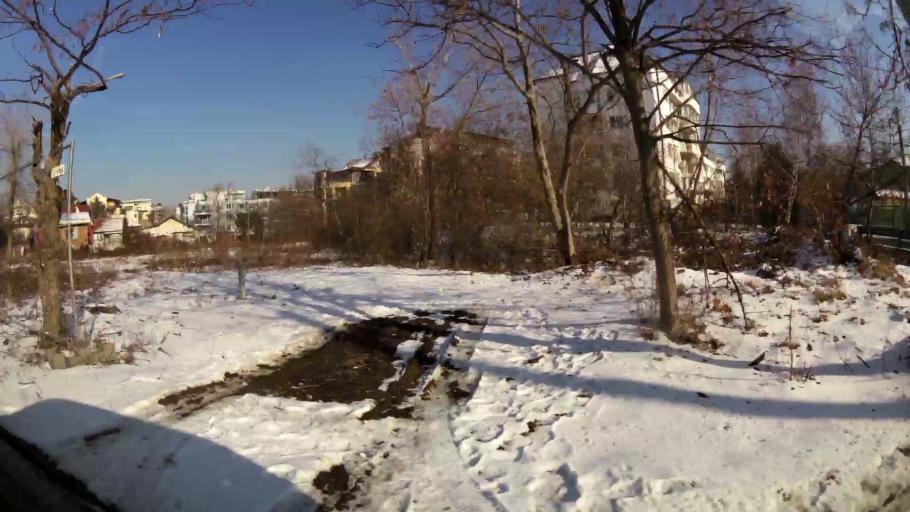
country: BG
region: Sofia-Capital
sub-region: Stolichna Obshtina
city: Sofia
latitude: 42.6529
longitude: 23.3333
